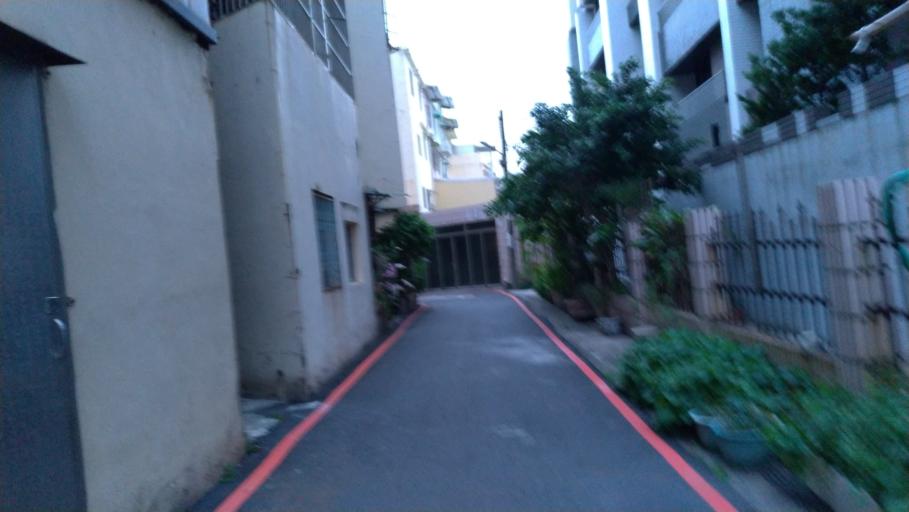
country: TW
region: Taiwan
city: Fengshan
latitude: 22.6533
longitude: 120.3632
